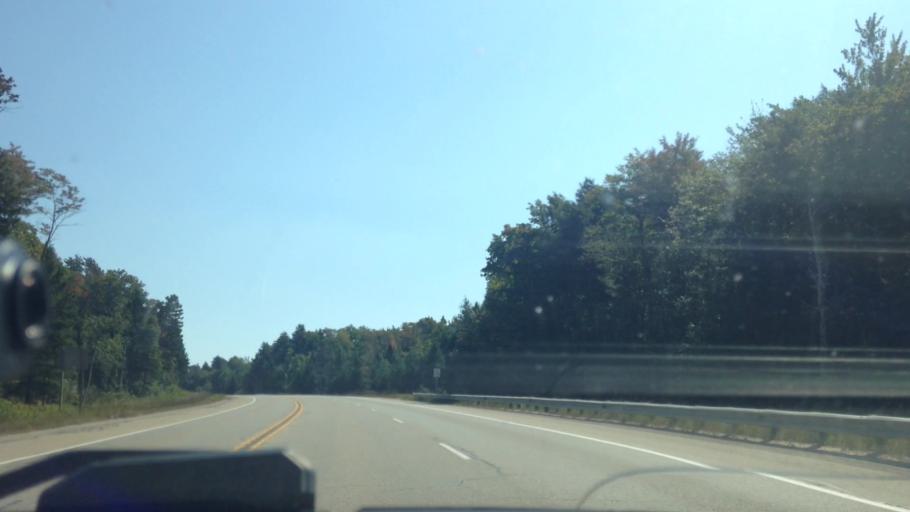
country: US
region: Michigan
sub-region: Alger County
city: Munising
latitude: 46.3896
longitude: -86.6463
